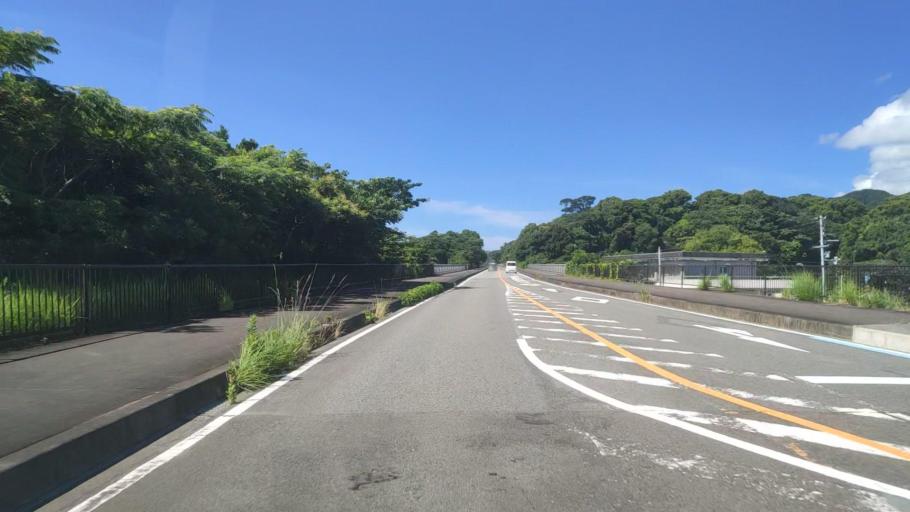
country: JP
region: Wakayama
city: Shingu
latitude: 33.7113
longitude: 135.9983
